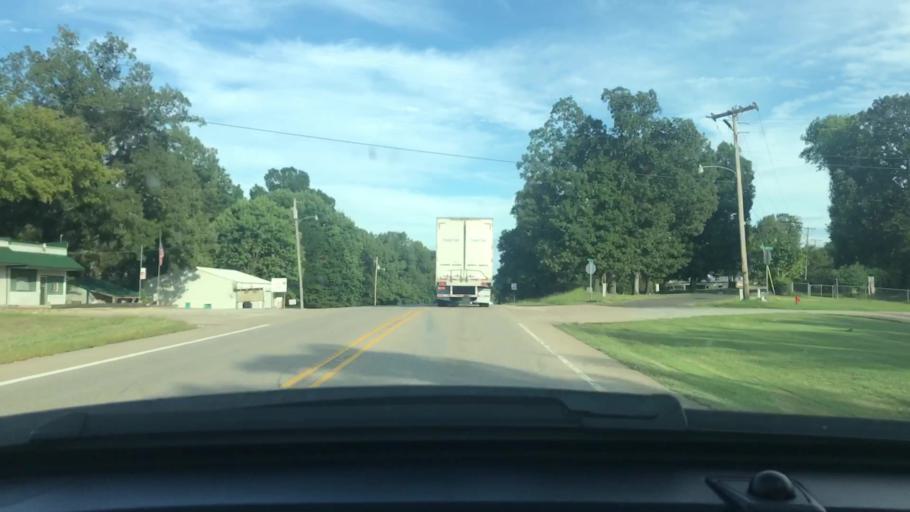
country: US
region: Arkansas
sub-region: Sharp County
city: Cherokee Village
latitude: 36.2390
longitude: -91.2598
